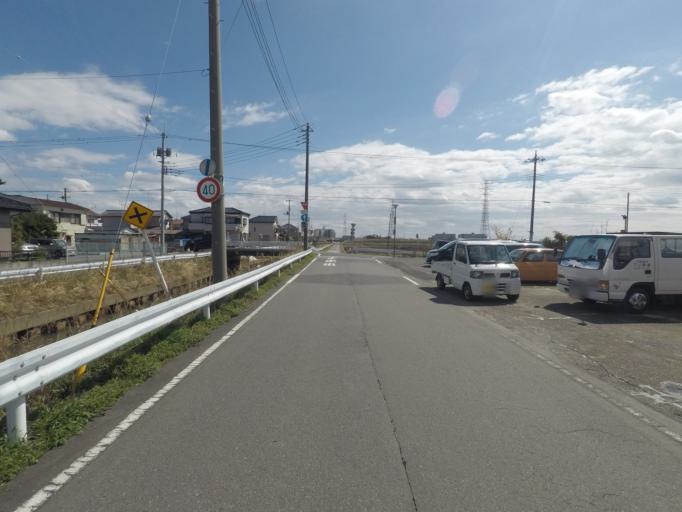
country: JP
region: Ibaraki
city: Fujishiro
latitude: 35.9352
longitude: 140.1185
